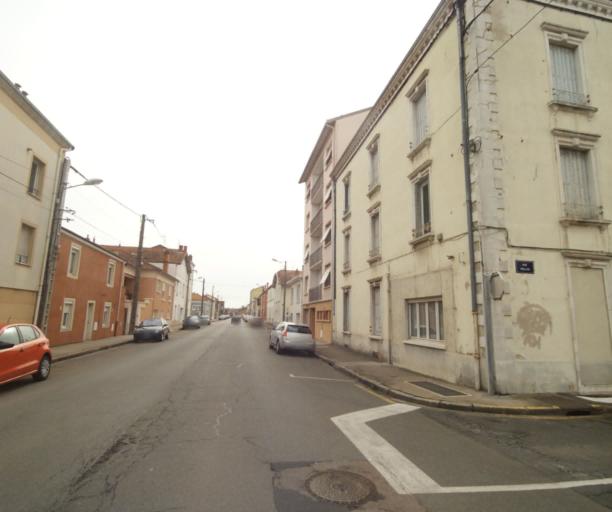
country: FR
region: Rhone-Alpes
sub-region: Departement de la Loire
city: Riorges
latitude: 46.0377
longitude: 4.0521
